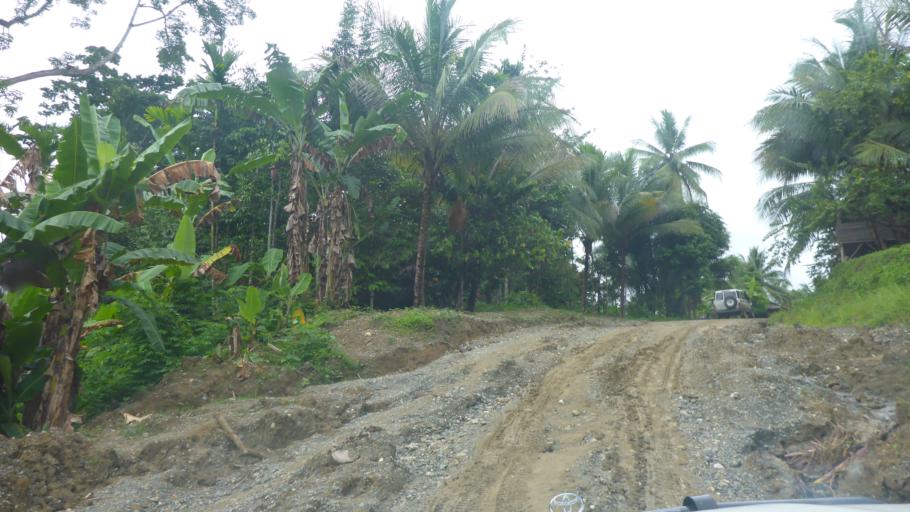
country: PG
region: Sandaun
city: Aitape
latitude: -3.5737
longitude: 142.8266
